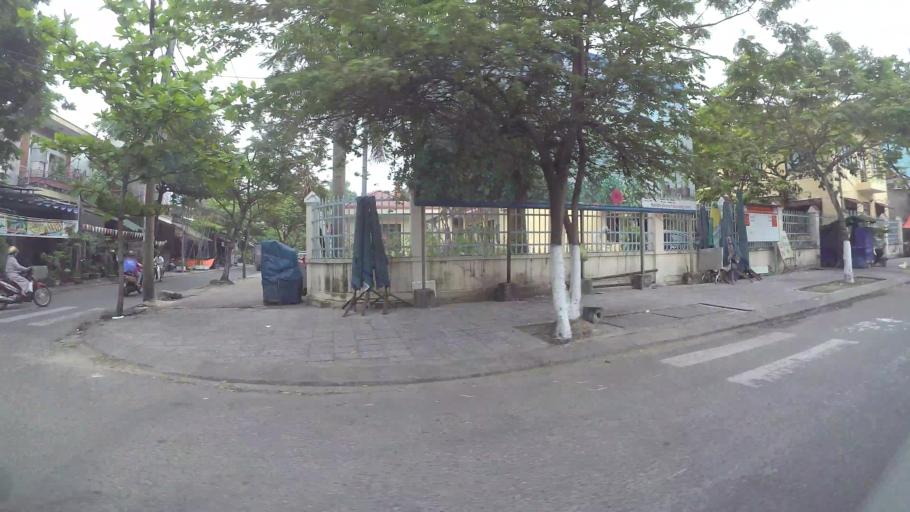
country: VN
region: Da Nang
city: Thanh Khe
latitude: 16.0595
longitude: 108.1870
